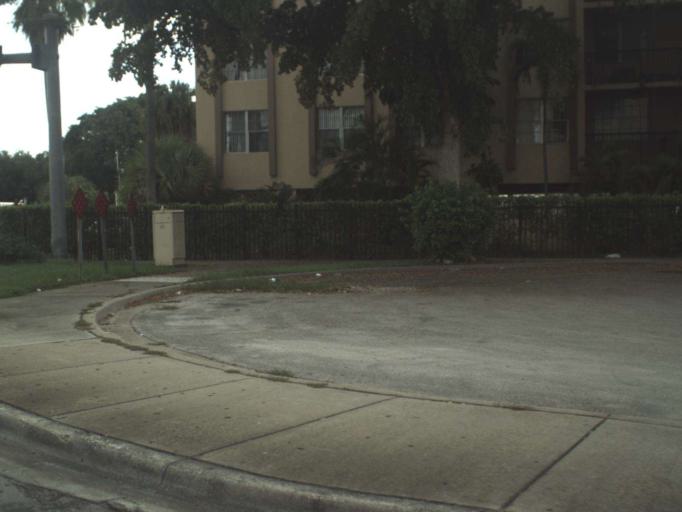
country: US
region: Florida
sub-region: Miami-Dade County
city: North Miami
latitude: 25.8995
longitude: -80.1790
